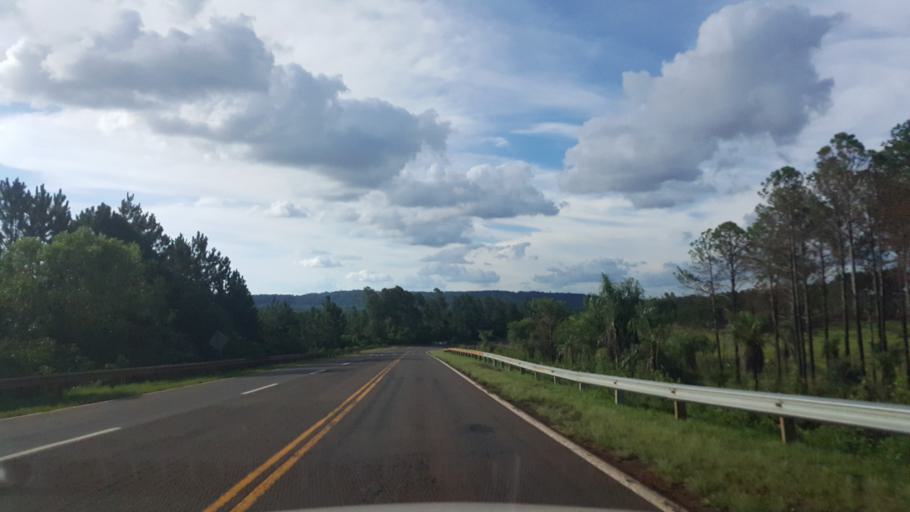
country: AR
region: Misiones
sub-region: Departamento de Candelaria
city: Loreto
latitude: -27.3255
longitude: -55.5439
